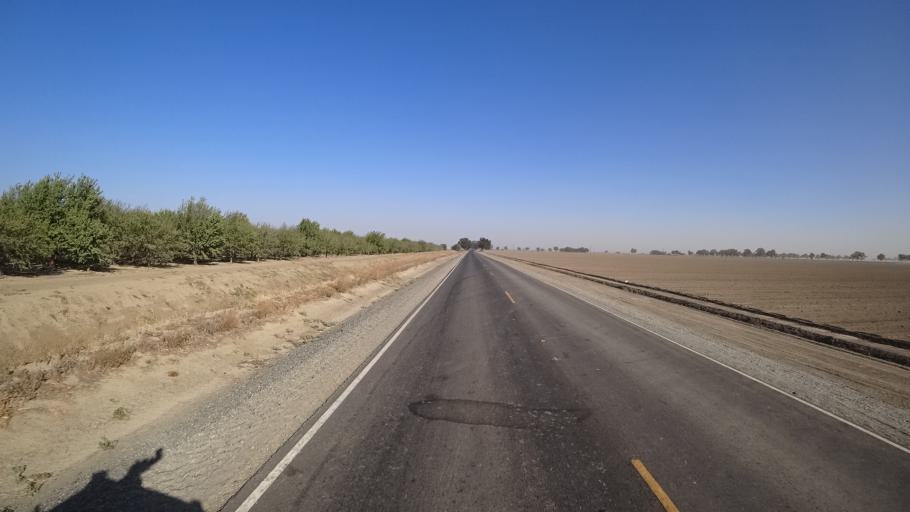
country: US
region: California
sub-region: Yolo County
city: Woodland
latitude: 38.7940
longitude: -121.8539
